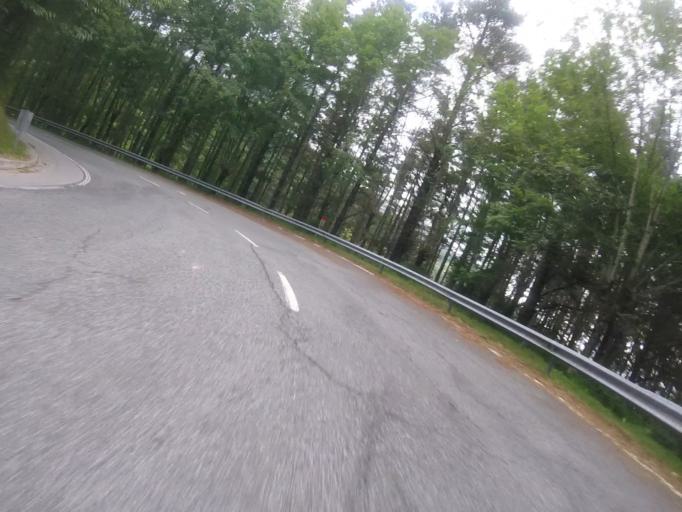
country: ES
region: Navarre
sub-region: Provincia de Navarra
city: Ezkurra
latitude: 43.0840
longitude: -1.8504
